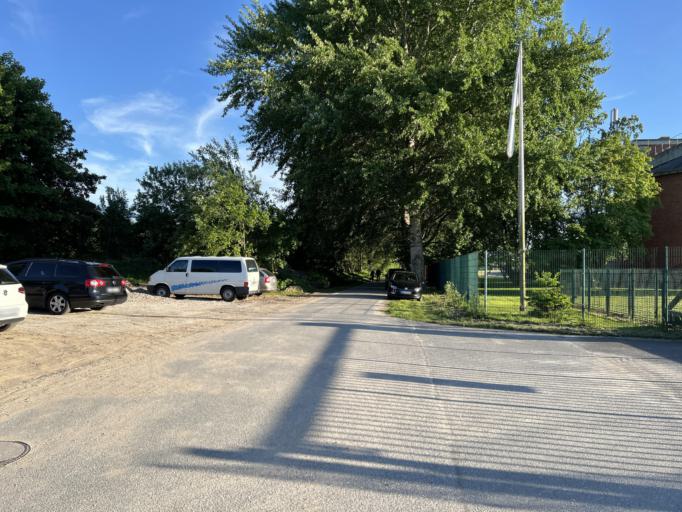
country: DE
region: Schleswig-Holstein
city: Wesseln
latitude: 54.1887
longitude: 9.0824
